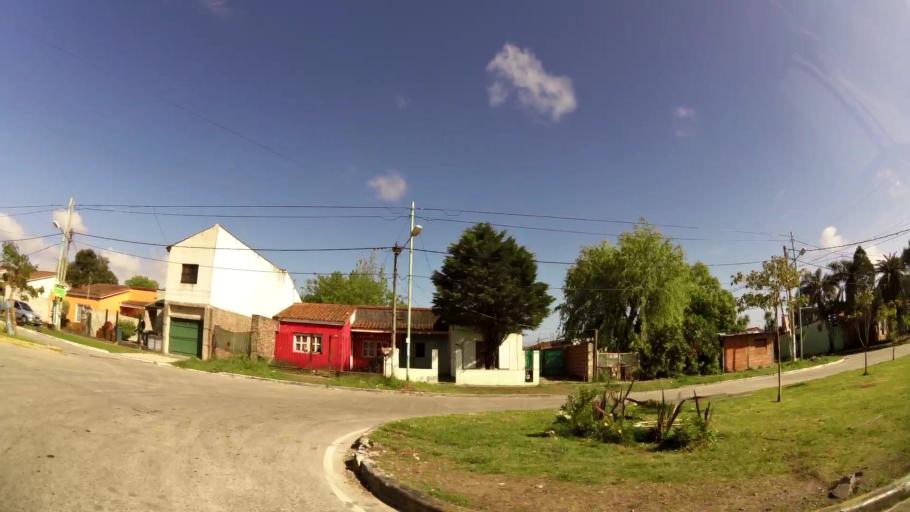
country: AR
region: Buenos Aires
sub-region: Partido de Quilmes
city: Quilmes
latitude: -34.7896
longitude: -58.1464
